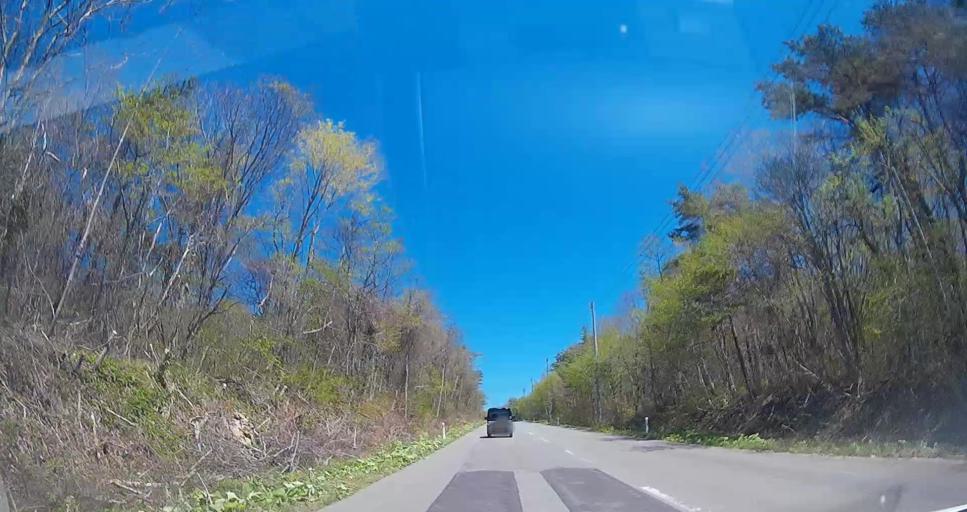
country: JP
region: Aomori
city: Mutsu
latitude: 41.2773
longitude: 141.3917
